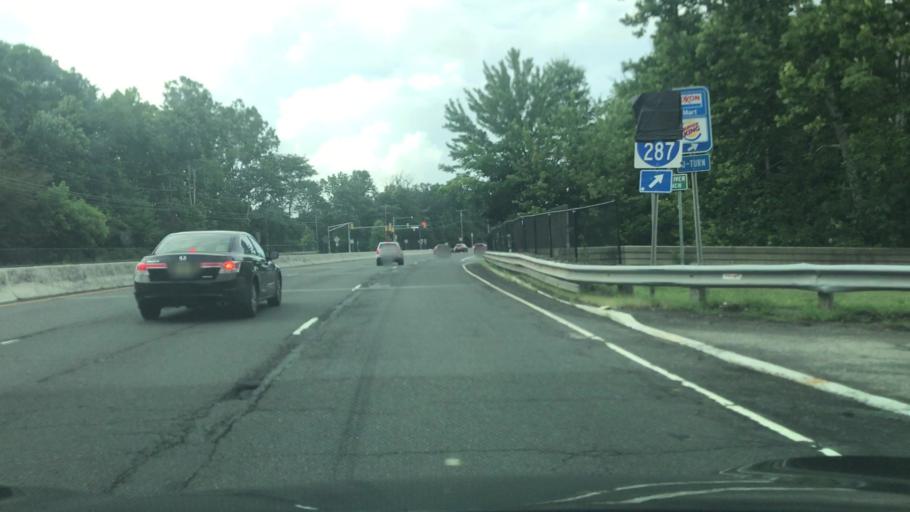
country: US
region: New Jersey
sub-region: Somerset County
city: Bedminster
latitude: 40.6609
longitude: -74.6456
